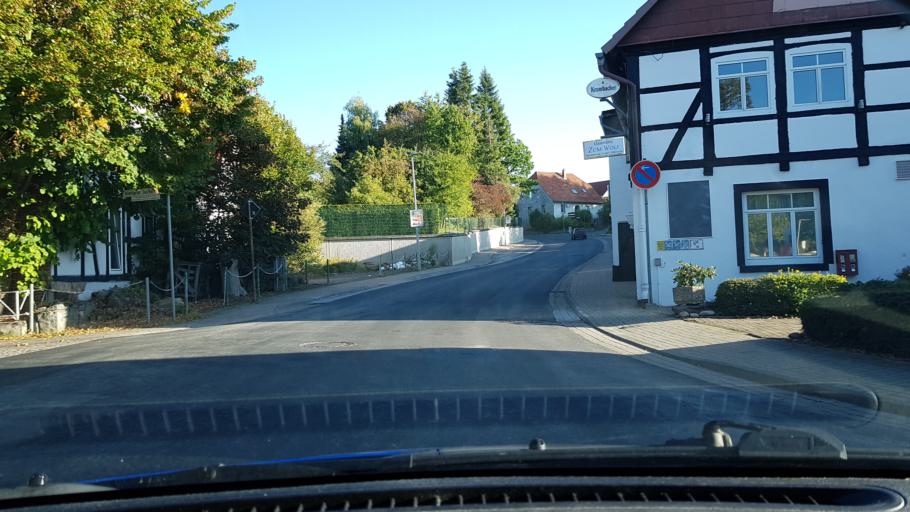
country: DE
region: Lower Saxony
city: Messenkamp
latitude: 52.2341
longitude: 9.4250
